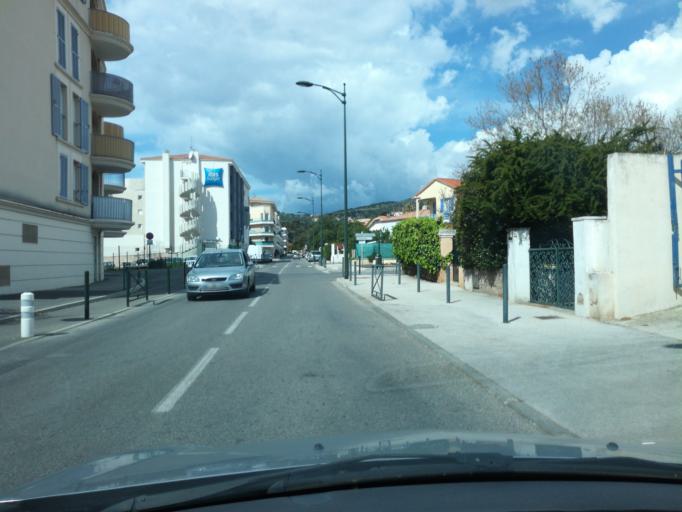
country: FR
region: Provence-Alpes-Cote d'Azur
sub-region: Departement du Var
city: Hyeres
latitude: 43.1199
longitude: 6.1410
